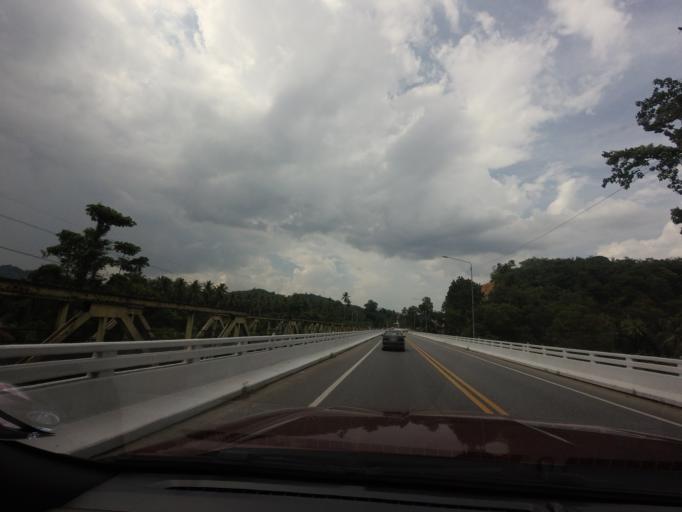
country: TH
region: Yala
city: Ban Nang Sata
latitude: 6.2779
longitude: 101.2894
